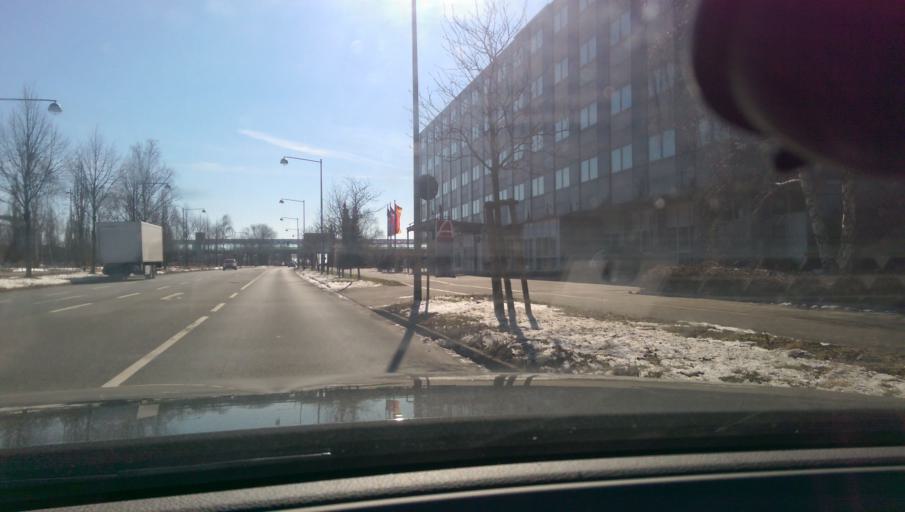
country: DE
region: Lower Saxony
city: Laatzen
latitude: 52.3206
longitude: 9.7963
